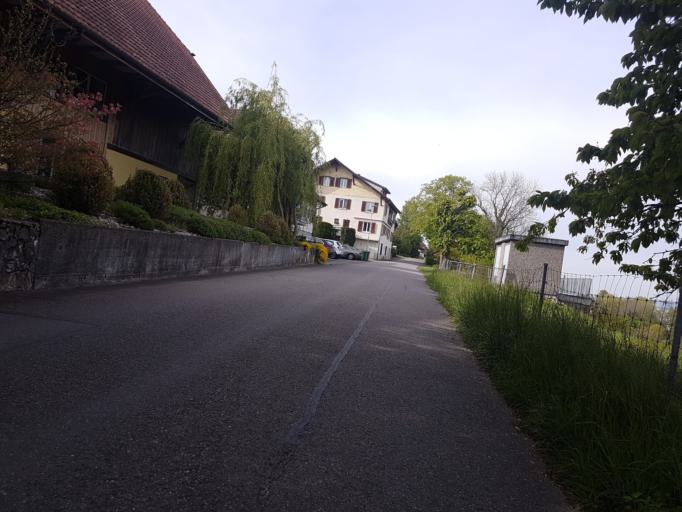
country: CH
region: Bern
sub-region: Seeland District
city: Tauffelen
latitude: 47.0985
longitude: 7.2113
